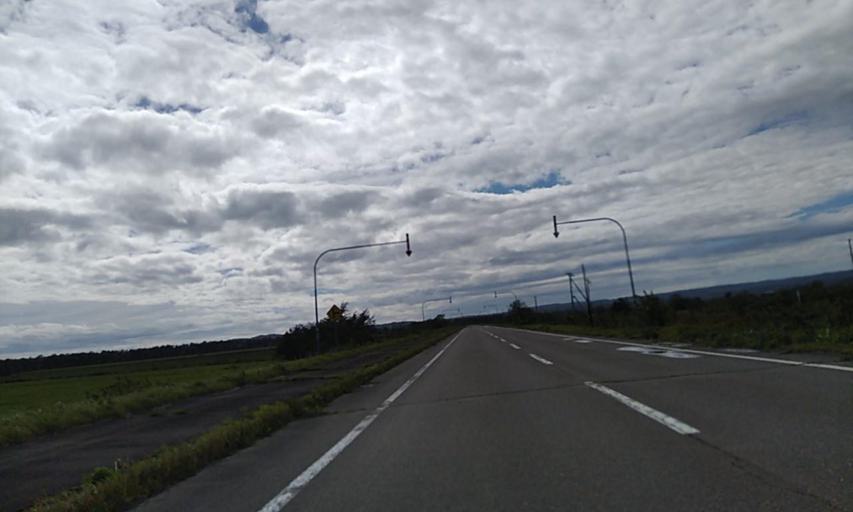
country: JP
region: Hokkaido
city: Obihiro
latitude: 42.7195
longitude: 143.6496
